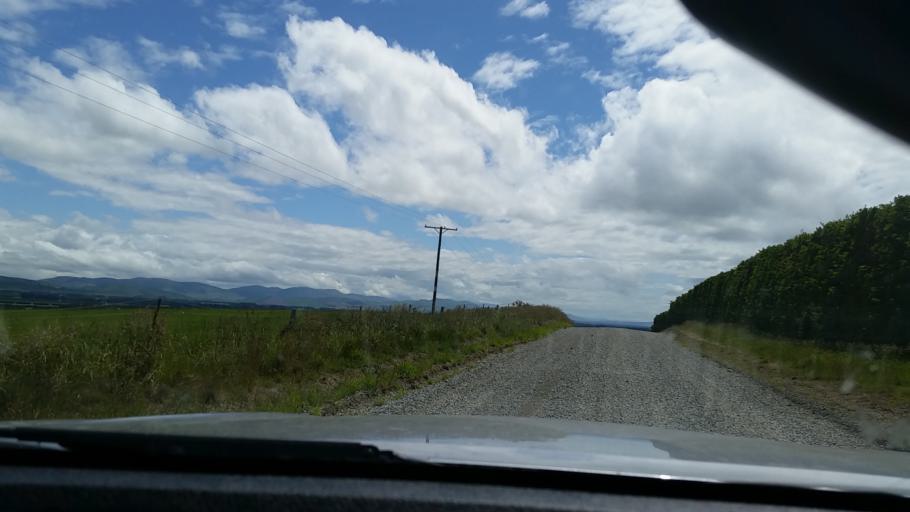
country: NZ
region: Southland
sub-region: Southland District
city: Winton
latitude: -45.8126
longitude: 168.5511
